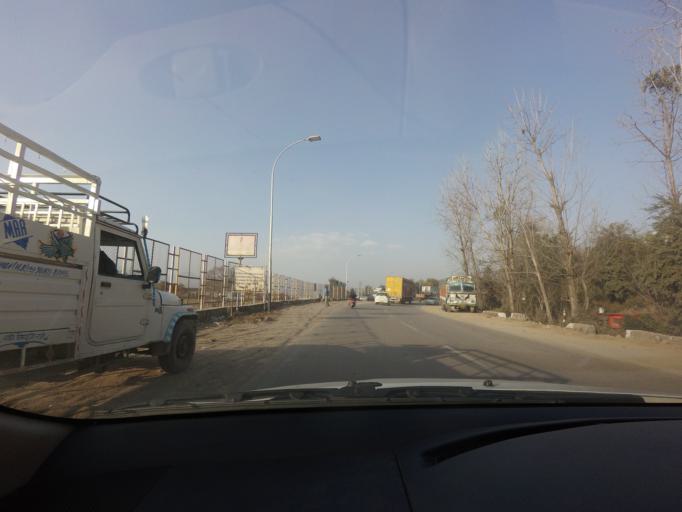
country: IN
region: Himachal Pradesh
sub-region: Mandi
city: Sundarnagar
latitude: 31.5391
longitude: 76.8950
